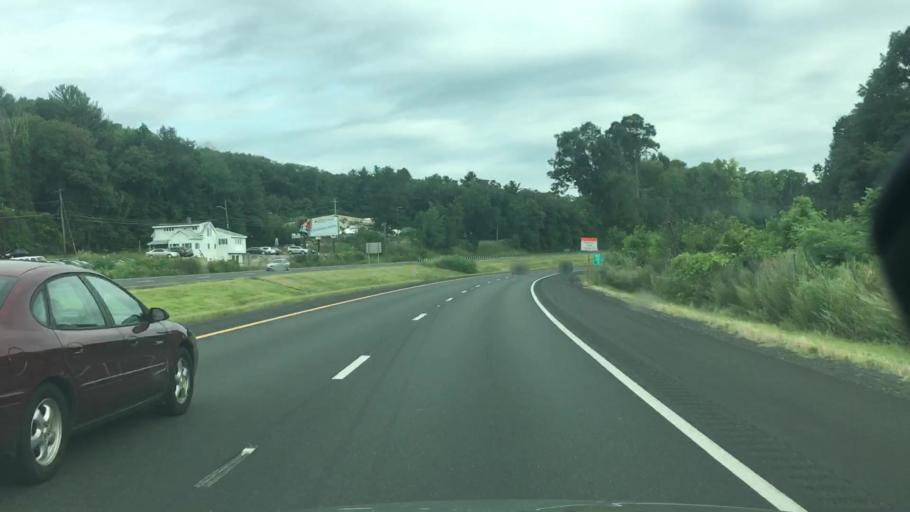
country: US
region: Massachusetts
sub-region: Hampshire County
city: Northampton
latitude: 42.3450
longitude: -72.6420
